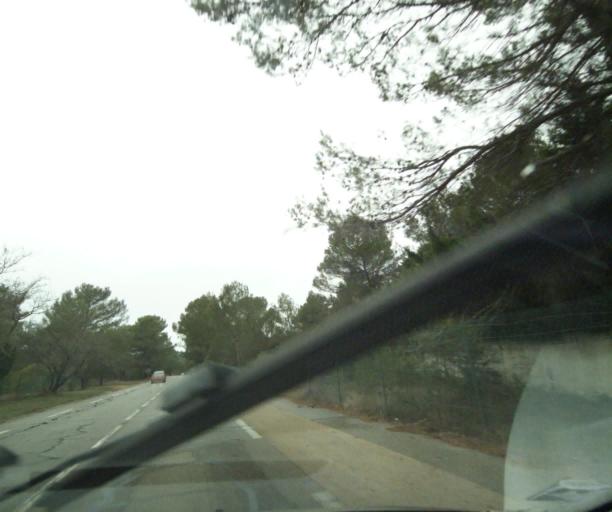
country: FR
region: Provence-Alpes-Cote d'Azur
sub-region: Departement des Bouches-du-Rhone
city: Le Puy-Sainte-Reparade
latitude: 43.6585
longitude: 5.4031
